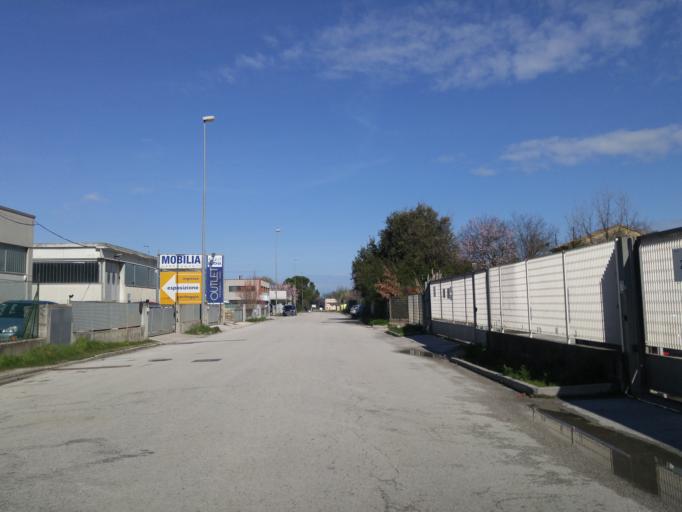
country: IT
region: The Marches
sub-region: Provincia di Pesaro e Urbino
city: Calcinelli
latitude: 43.7441
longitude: 12.9182
